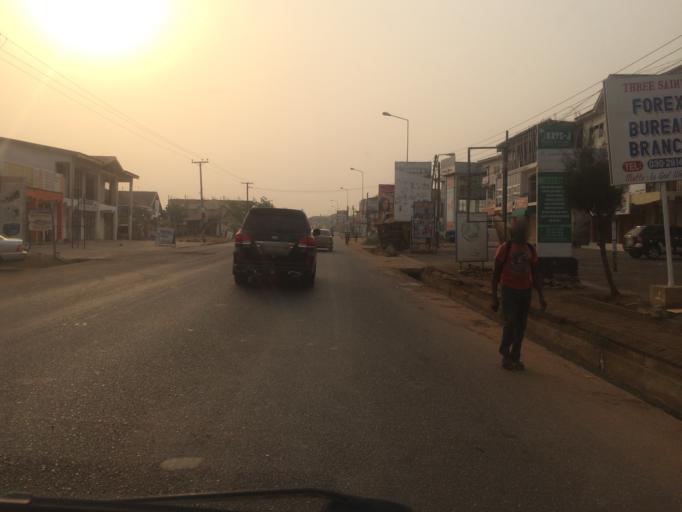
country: GH
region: Greater Accra
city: Nungua
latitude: 5.6397
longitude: -0.1069
